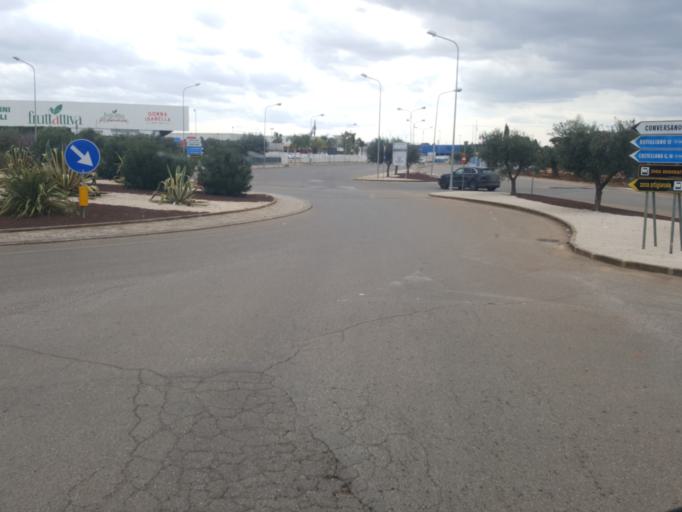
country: IT
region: Apulia
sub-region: Provincia di Bari
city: Conversano
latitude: 40.9806
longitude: 17.1183
